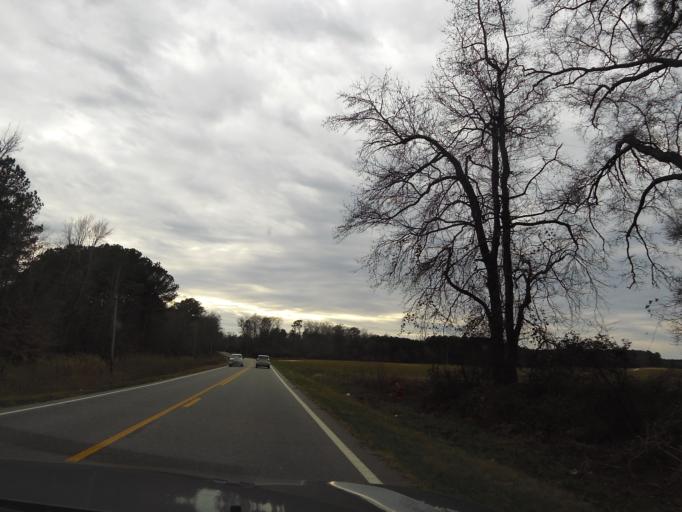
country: US
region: North Carolina
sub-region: Edgecombe County
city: Tarboro
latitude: 36.0045
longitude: -77.5504
